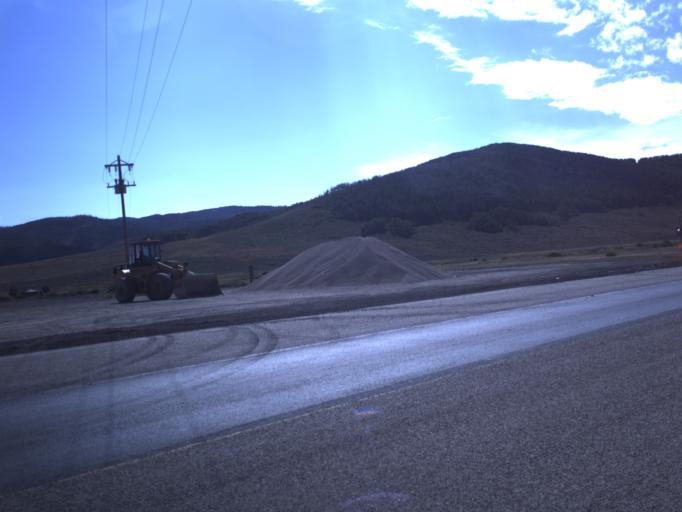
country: US
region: Utah
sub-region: Wasatch County
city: Heber
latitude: 40.2414
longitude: -111.1822
